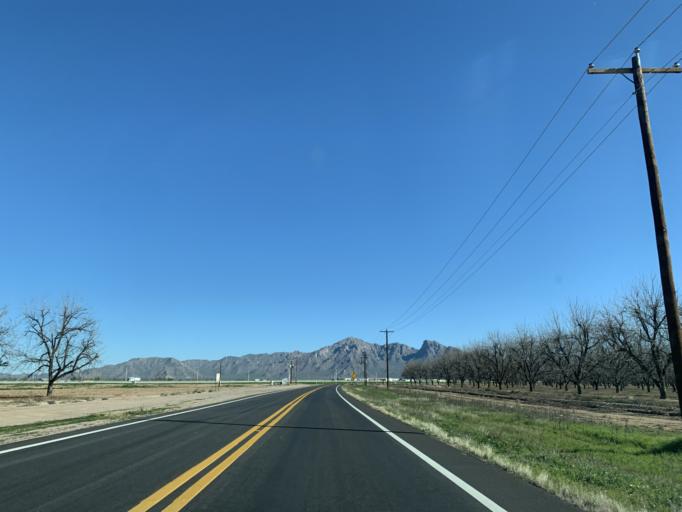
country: US
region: Arizona
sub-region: Pinal County
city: Eloy
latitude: 32.7196
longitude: -111.5137
